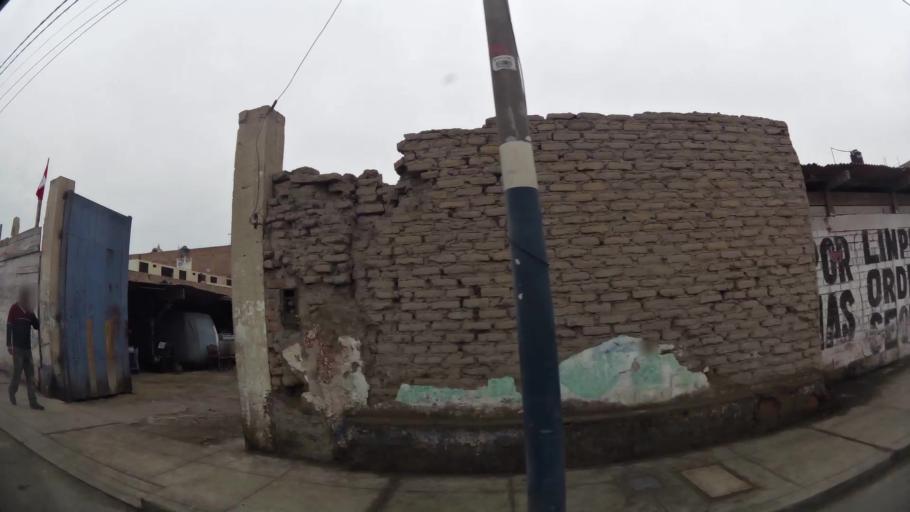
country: PE
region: Ica
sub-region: Provincia de Pisco
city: Pisco
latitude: -13.7089
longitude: -76.2015
